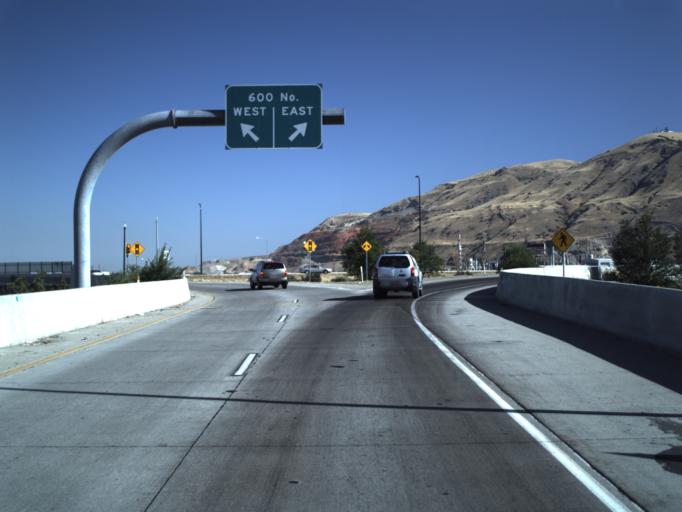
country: US
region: Utah
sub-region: Salt Lake County
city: Salt Lake City
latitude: 40.7811
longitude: -111.9100
